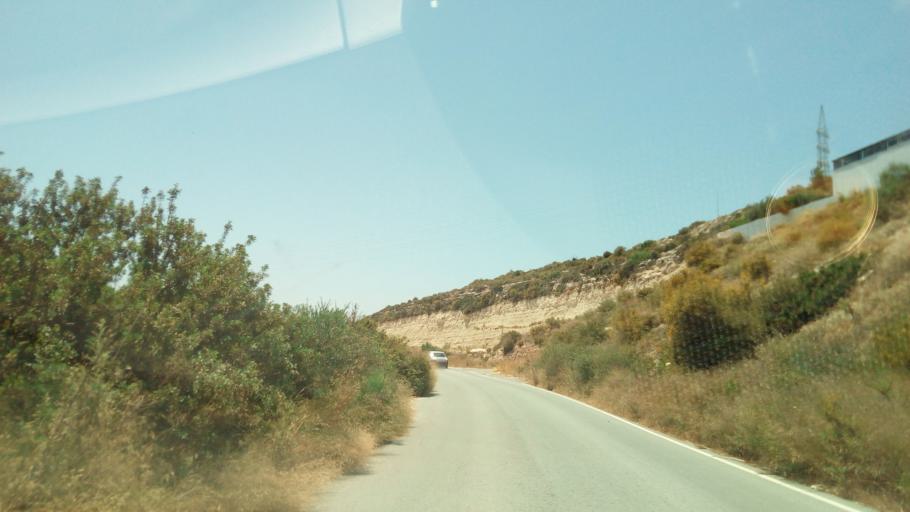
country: CY
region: Limassol
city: Ypsonas
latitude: 34.7228
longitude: 32.9528
